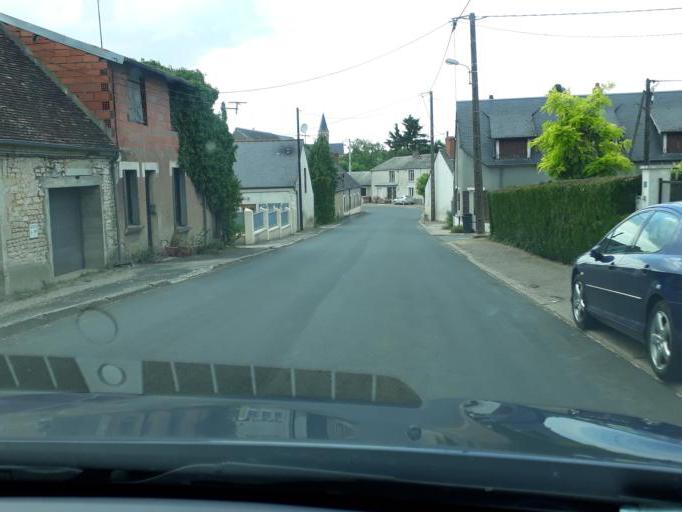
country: FR
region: Centre
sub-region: Departement du Cher
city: Baugy
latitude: 47.0949
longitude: 2.6778
